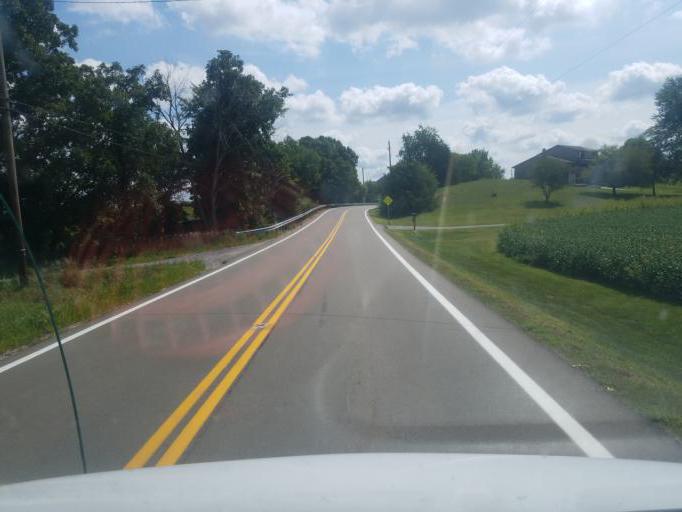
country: US
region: Ohio
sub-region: Marion County
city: Prospect
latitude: 40.3940
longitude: -83.1574
